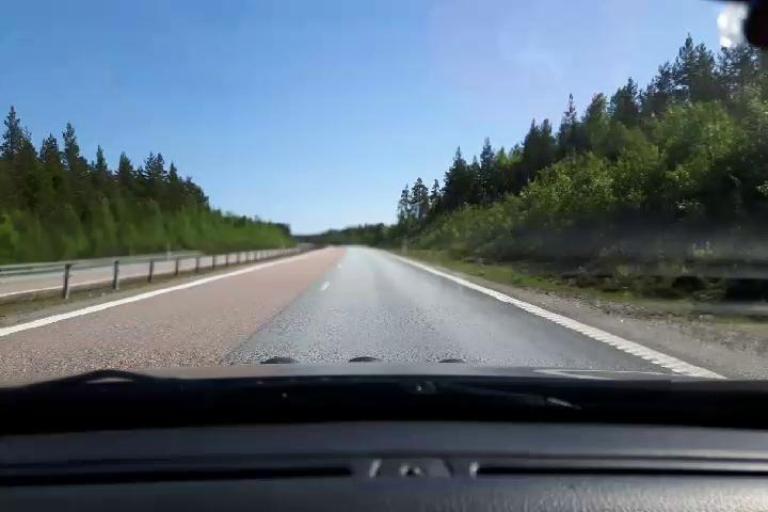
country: SE
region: Gaevleborg
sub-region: Soderhamns Kommun
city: Soderhamn
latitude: 61.4198
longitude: 16.9860
